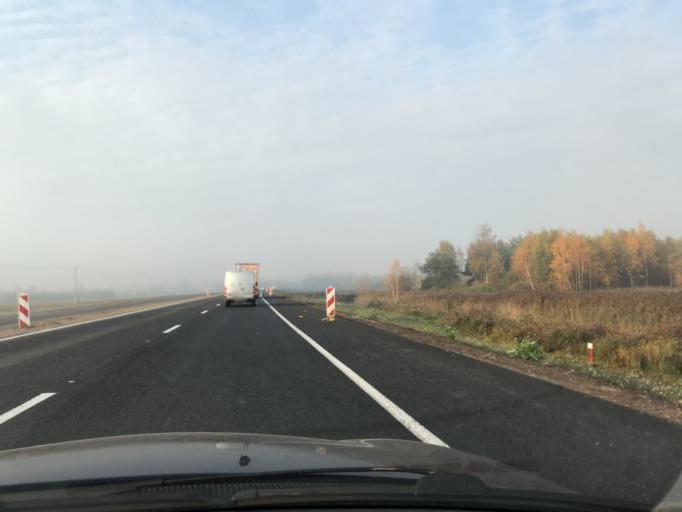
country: BY
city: Berezovka
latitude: 53.8335
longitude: 25.4598
